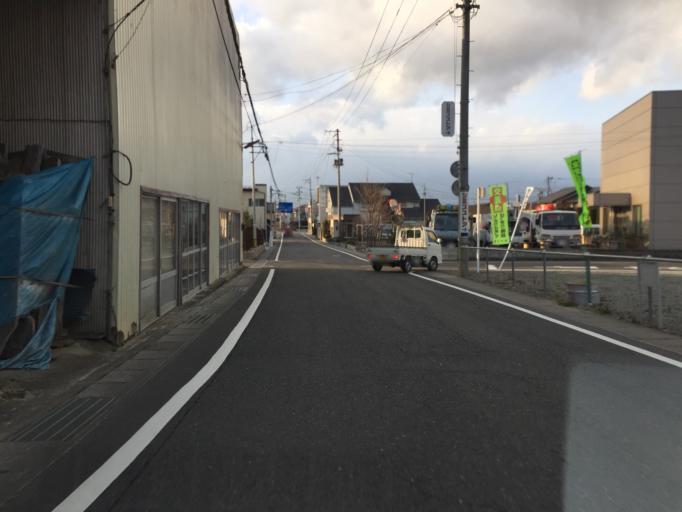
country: JP
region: Fukushima
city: Motomiya
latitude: 37.5132
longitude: 140.4083
